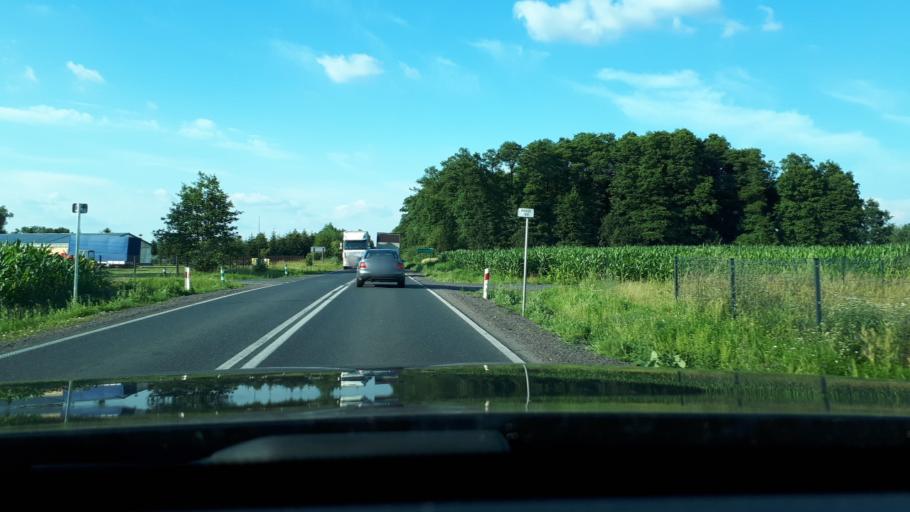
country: PL
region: Masovian Voivodeship
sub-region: Powiat plonski
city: Sochocin
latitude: 52.7251
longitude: 20.5091
